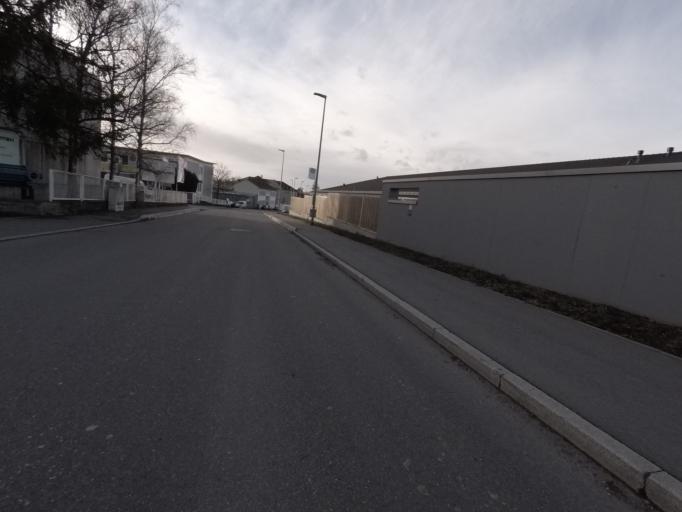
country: DE
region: Baden-Wuerttemberg
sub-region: Tuebingen Region
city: Pfullingen
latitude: 48.4863
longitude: 9.2298
